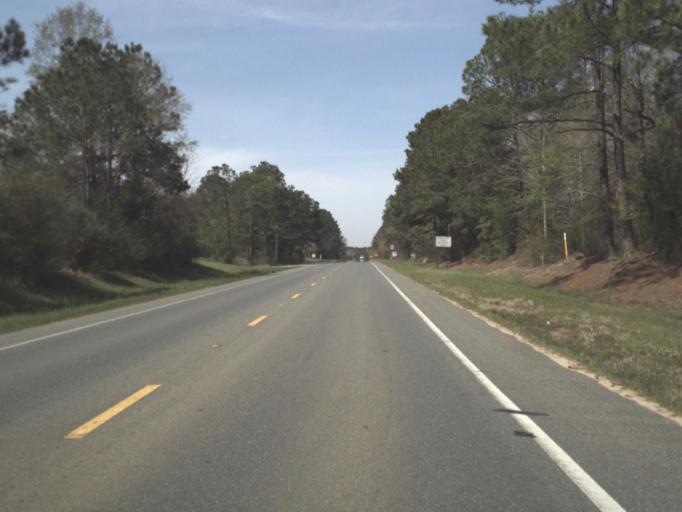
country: US
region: Florida
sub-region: Holmes County
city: Bonifay
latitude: 30.7793
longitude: -85.6301
